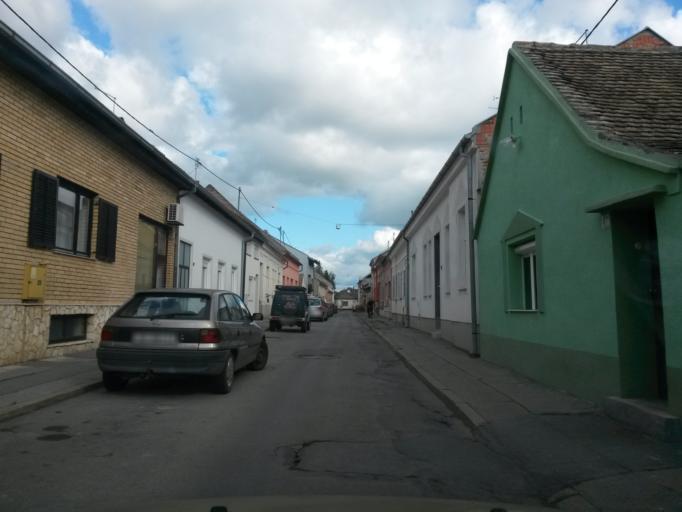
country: HR
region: Osjecko-Baranjska
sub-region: Grad Osijek
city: Osijek
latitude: 45.5591
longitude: 18.7213
